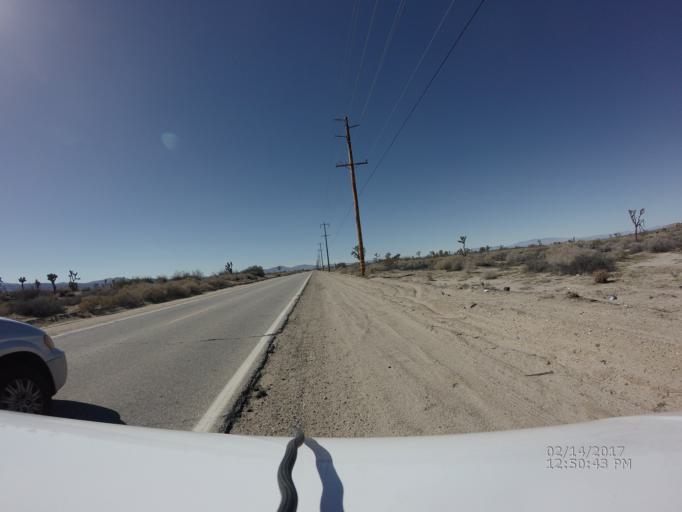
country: US
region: California
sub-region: Los Angeles County
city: Lake Los Angeles
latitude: 34.5801
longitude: -117.8869
